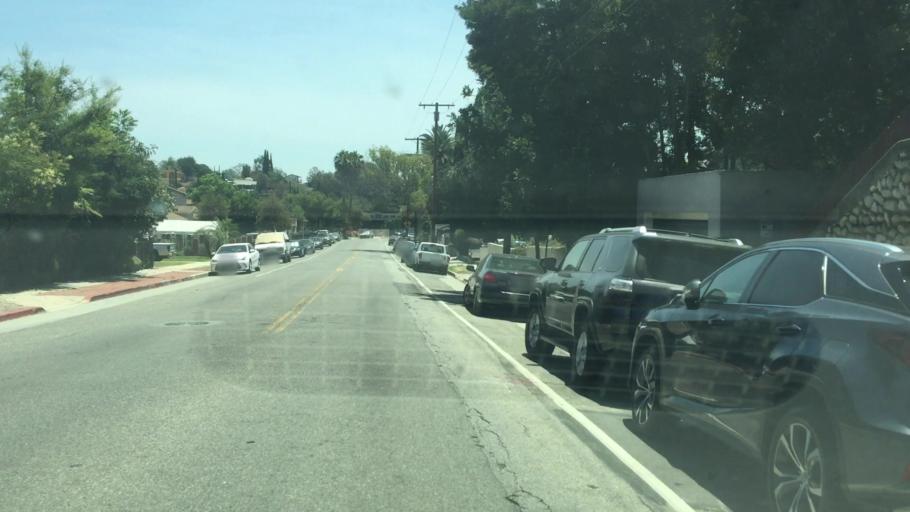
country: US
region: California
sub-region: Los Angeles County
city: Glendale
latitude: 34.1163
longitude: -118.2137
